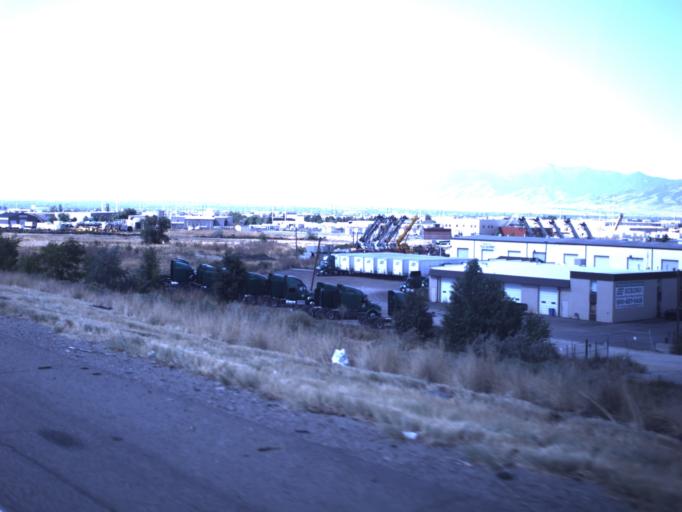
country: US
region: Utah
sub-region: Salt Lake County
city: Salt Lake City
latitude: 40.7516
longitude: -111.9488
